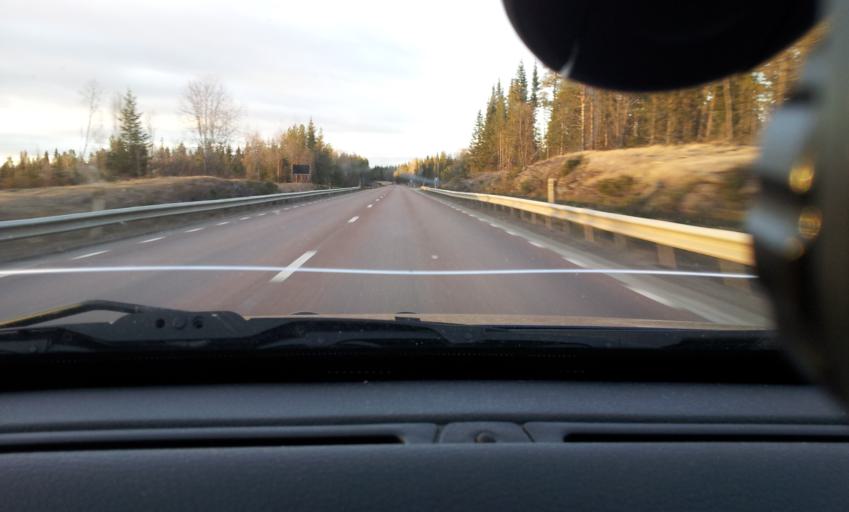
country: SE
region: Jaemtland
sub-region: Bergs Kommun
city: Hoverberg
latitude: 62.9345
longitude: 14.5399
